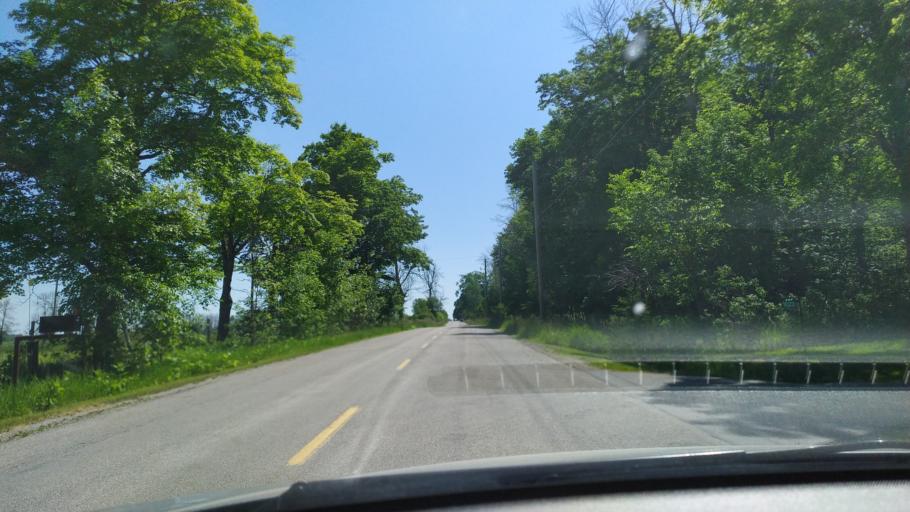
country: CA
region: Ontario
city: Waterloo
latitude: 43.4680
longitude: -80.6575
